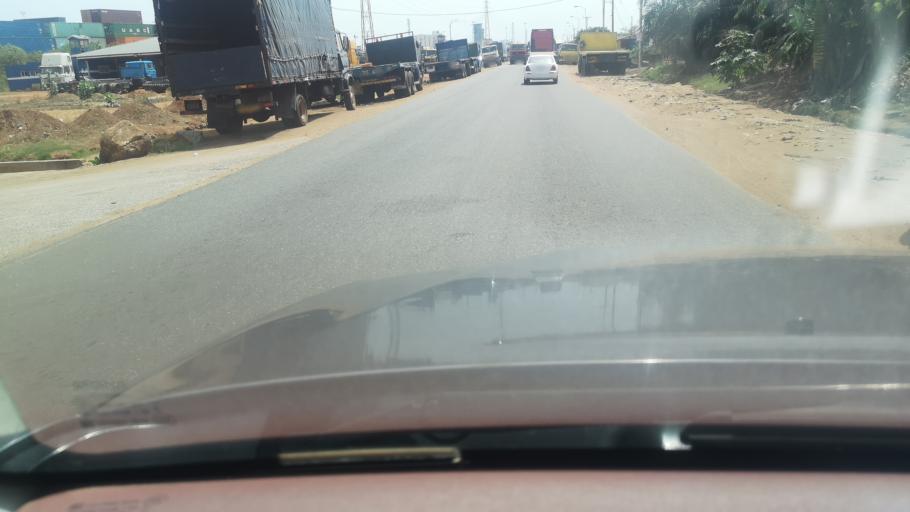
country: GH
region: Greater Accra
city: Tema
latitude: 5.6296
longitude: -0.0083
